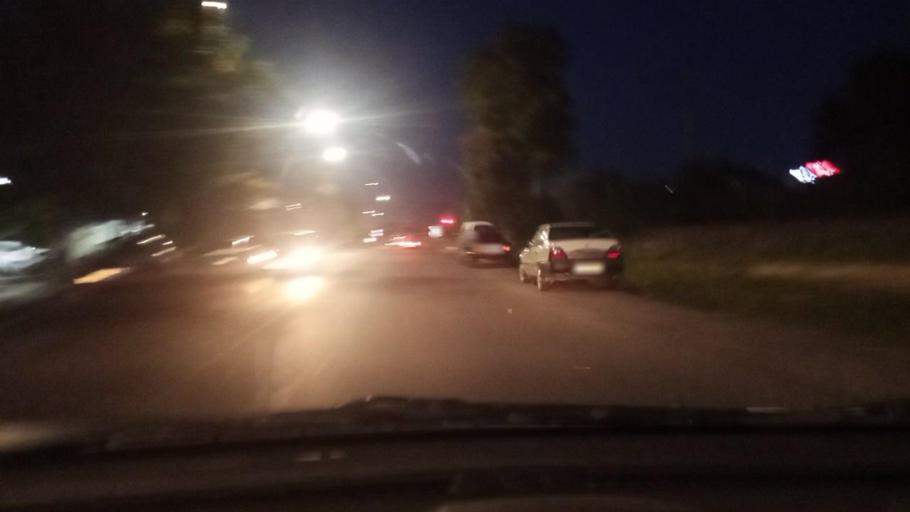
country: UZ
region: Toshkent Shahri
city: Tashkent
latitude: 41.2686
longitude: 69.2693
